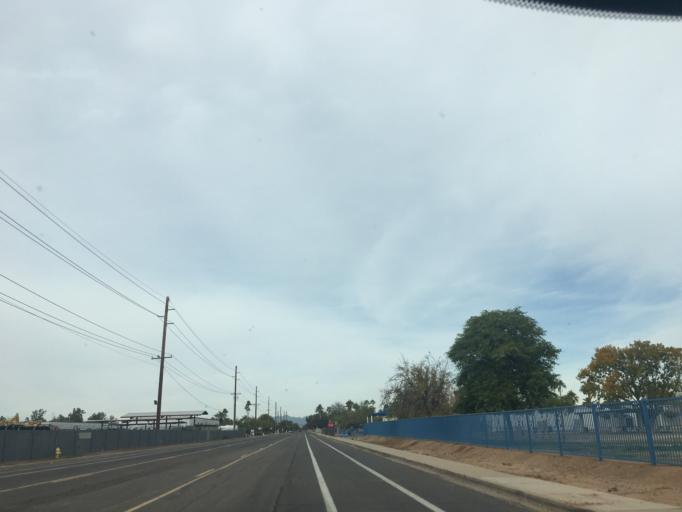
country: US
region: Arizona
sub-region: Maricopa County
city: Gilbert
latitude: 33.3586
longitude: -111.7984
